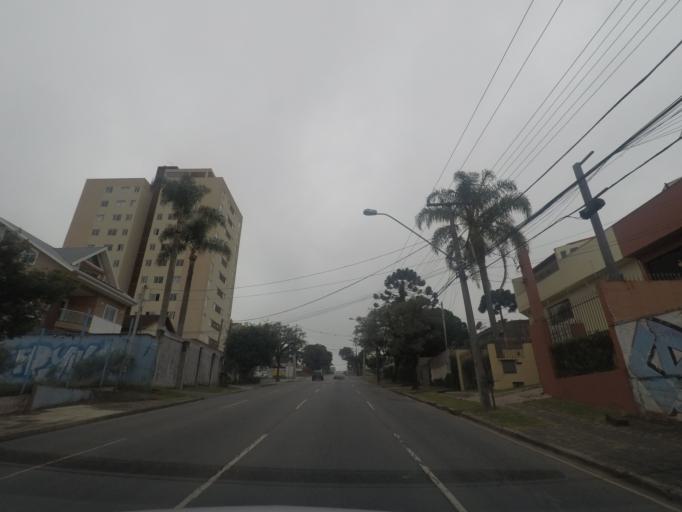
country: BR
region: Parana
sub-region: Curitiba
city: Curitiba
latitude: -25.3816
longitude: -49.2272
